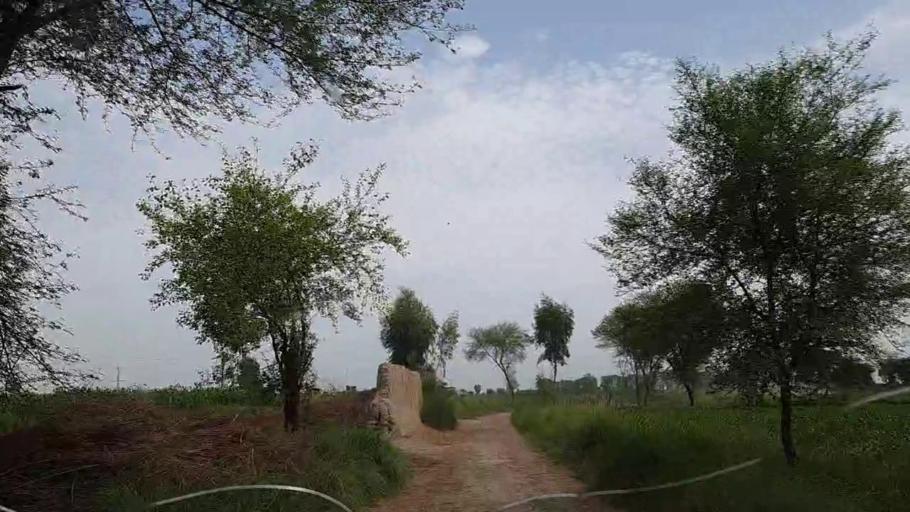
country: PK
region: Sindh
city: Tharu Shah
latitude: 26.8945
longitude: 68.0694
